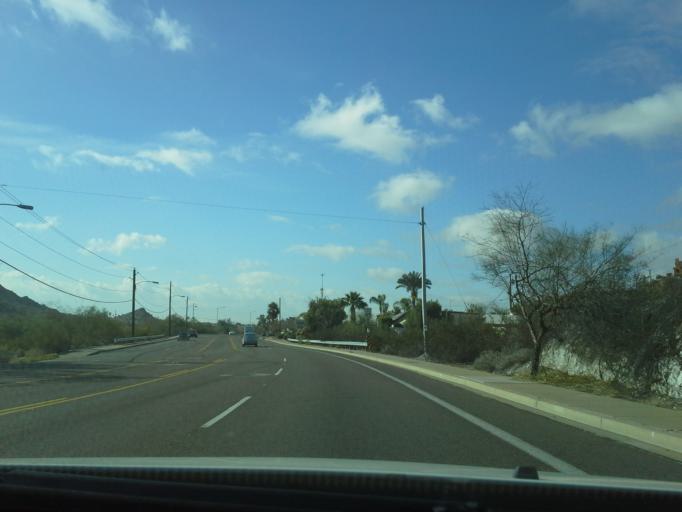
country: US
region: Arizona
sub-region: Maricopa County
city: Paradise Valley
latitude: 33.5930
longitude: -112.0422
